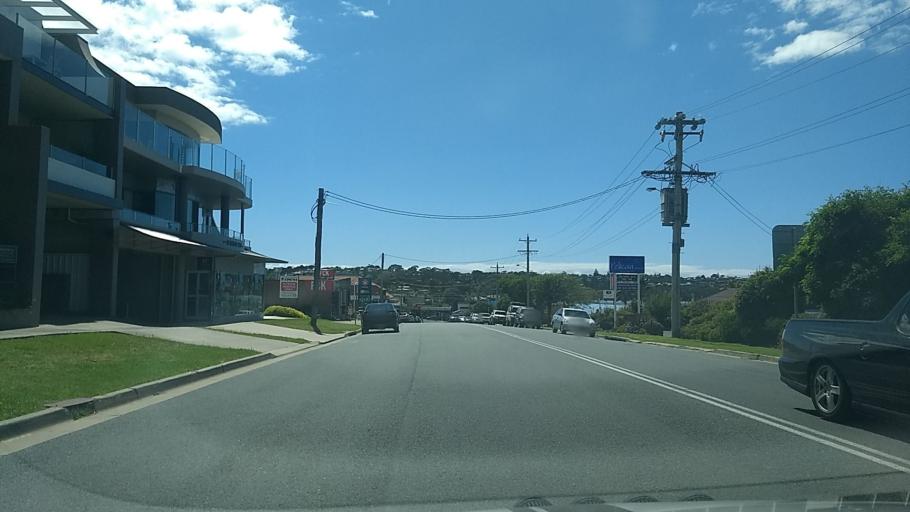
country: AU
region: New South Wales
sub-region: Bega Valley
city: Merimbula
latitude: -36.8879
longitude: 149.9077
